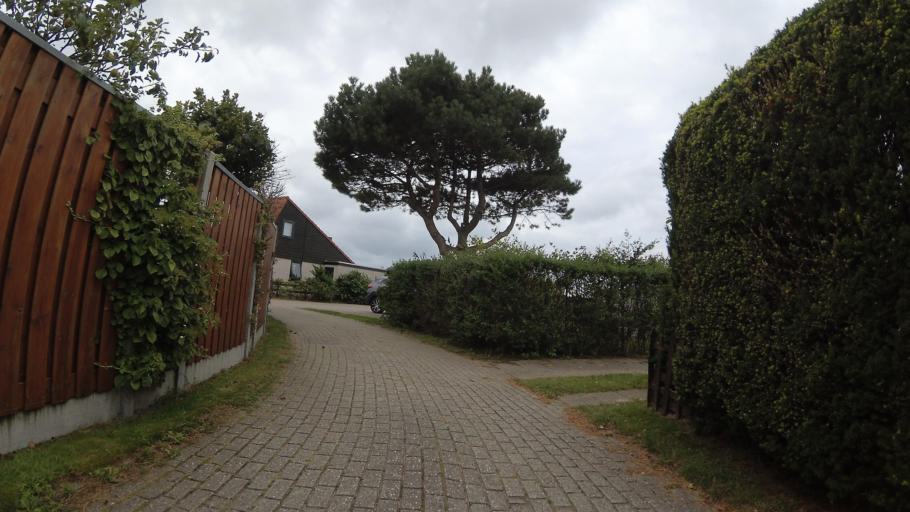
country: NL
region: North Holland
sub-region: Gemeente Den Helder
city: Den Helder
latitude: 52.9019
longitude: 4.7343
